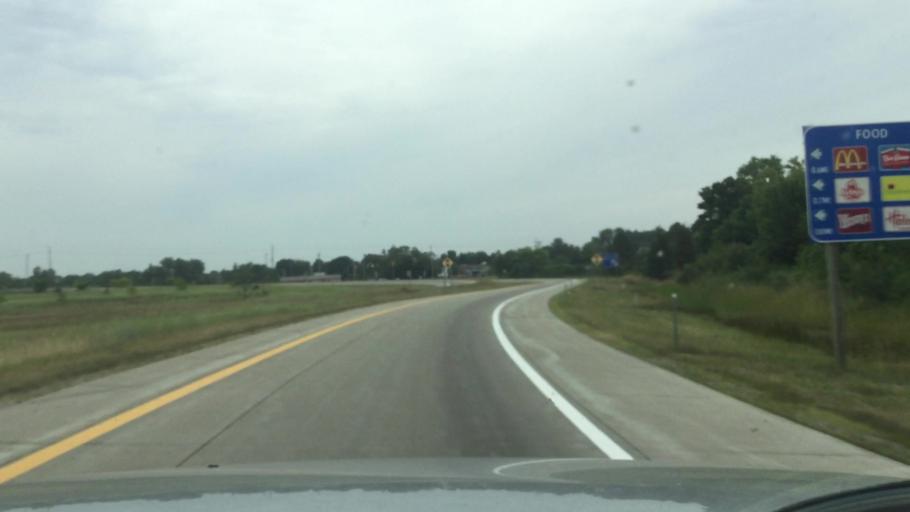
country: US
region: Michigan
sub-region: Genesee County
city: Grand Blanc
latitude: 42.9415
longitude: -83.6806
